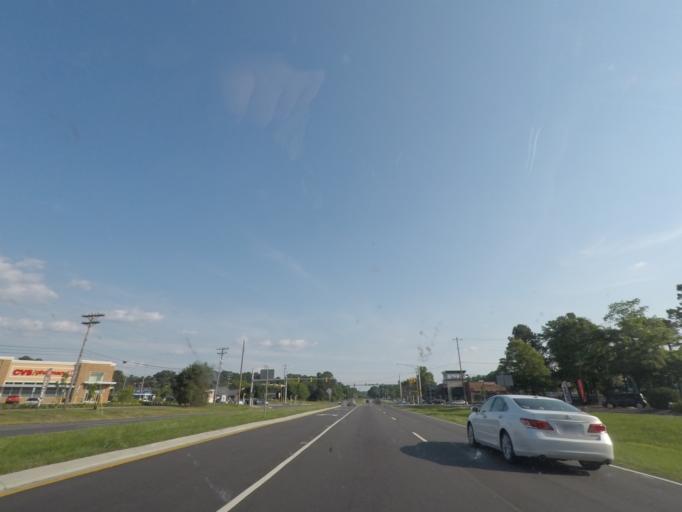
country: US
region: North Carolina
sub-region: Orange County
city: Chapel Hill
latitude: 35.9373
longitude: -79.0235
